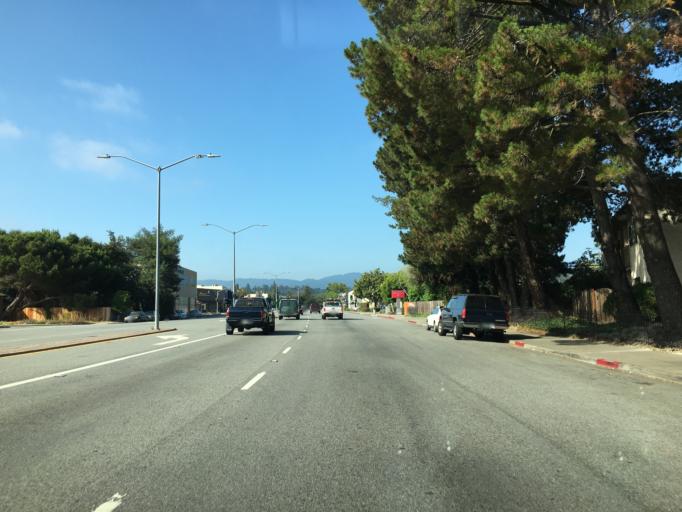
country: US
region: California
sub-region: San Mateo County
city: Redwood City
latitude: 37.4586
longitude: -122.2269
